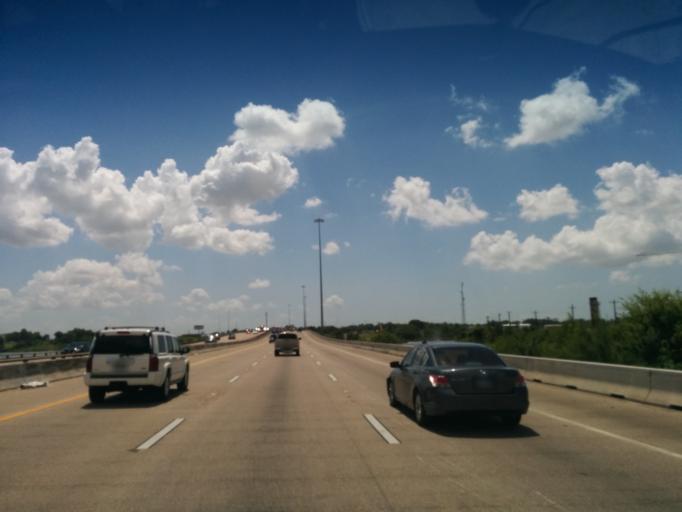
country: US
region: Texas
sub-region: Harris County
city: Highlands
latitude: 29.7943
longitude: -95.0653
